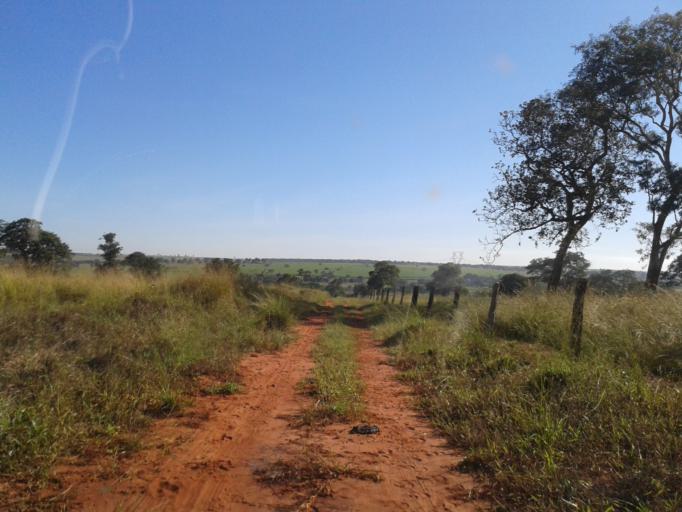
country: BR
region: Minas Gerais
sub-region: Santa Vitoria
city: Santa Vitoria
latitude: -19.0081
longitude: -50.3179
